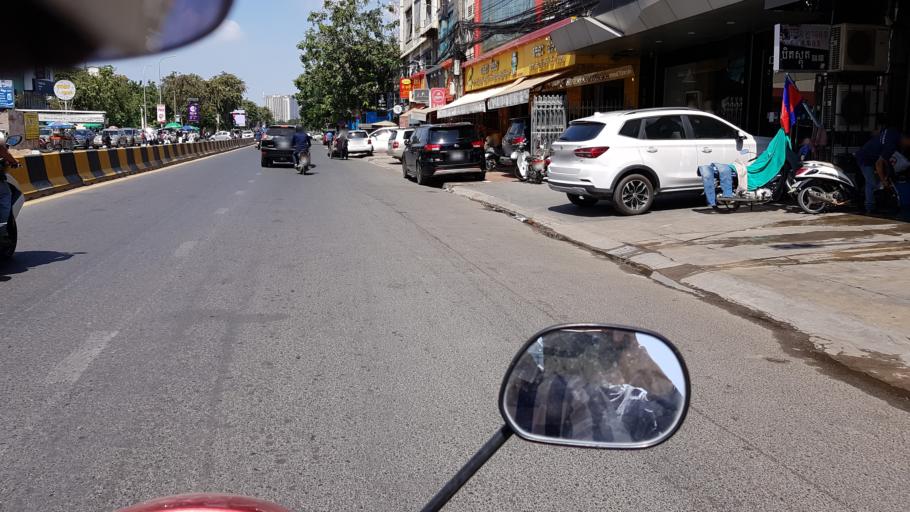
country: KH
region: Phnom Penh
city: Phnom Penh
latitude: 11.5663
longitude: 104.9117
